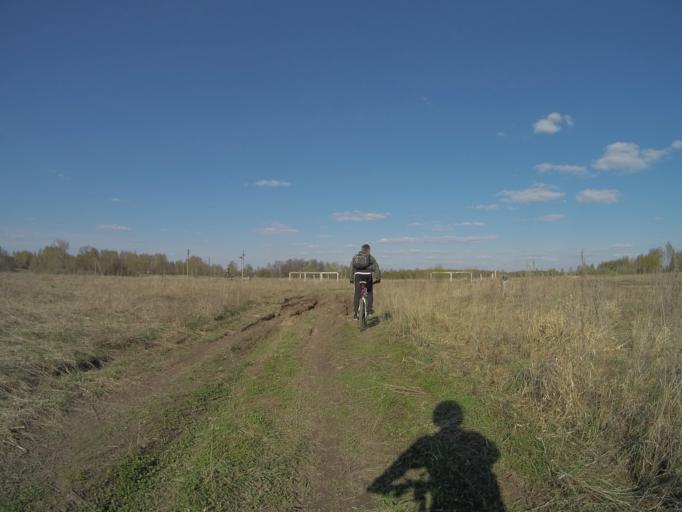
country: RU
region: Vladimir
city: Orgtrud
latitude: 56.3474
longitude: 40.6854
